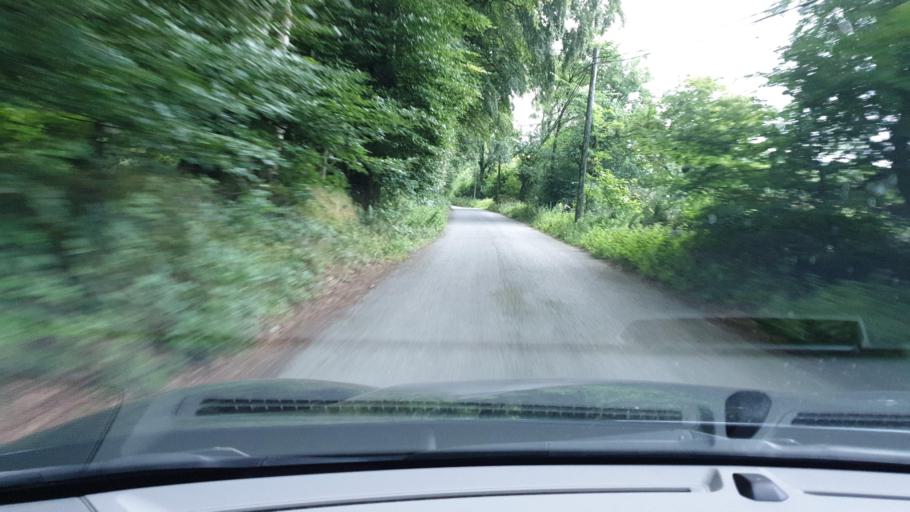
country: IE
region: Leinster
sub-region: South Dublin
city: Rathcoole
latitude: 53.2168
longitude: -6.4805
